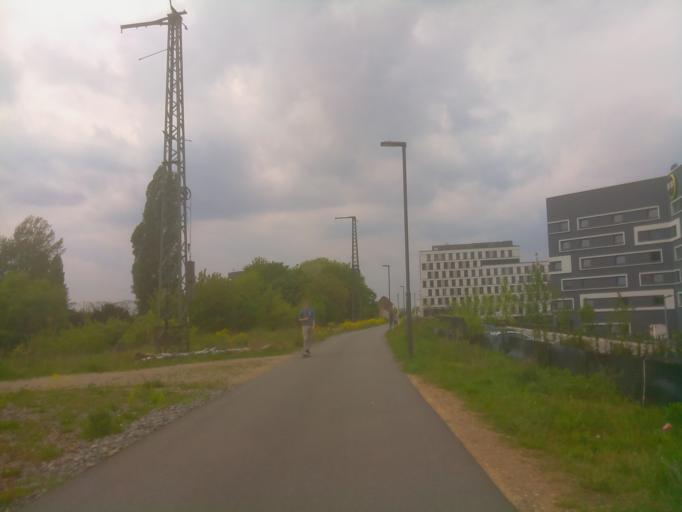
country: DE
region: Baden-Wuerttemberg
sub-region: Karlsruhe Region
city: Heidelberg
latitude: 49.3965
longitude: 8.6756
